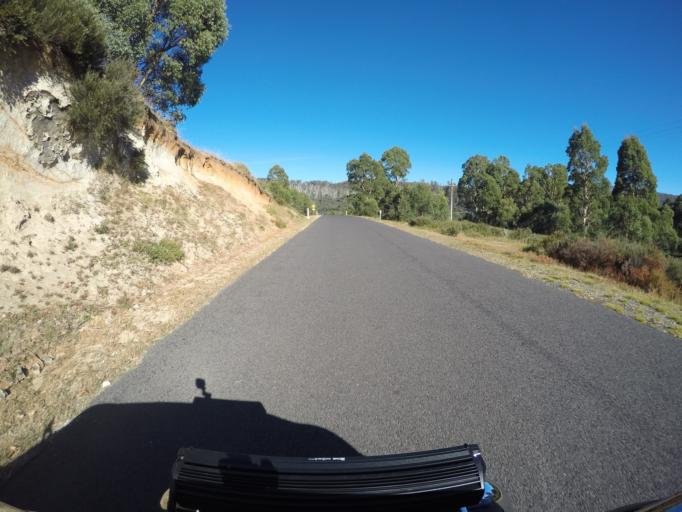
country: AU
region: New South Wales
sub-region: Snowy River
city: Jindabyne
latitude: -36.0495
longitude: 148.2813
